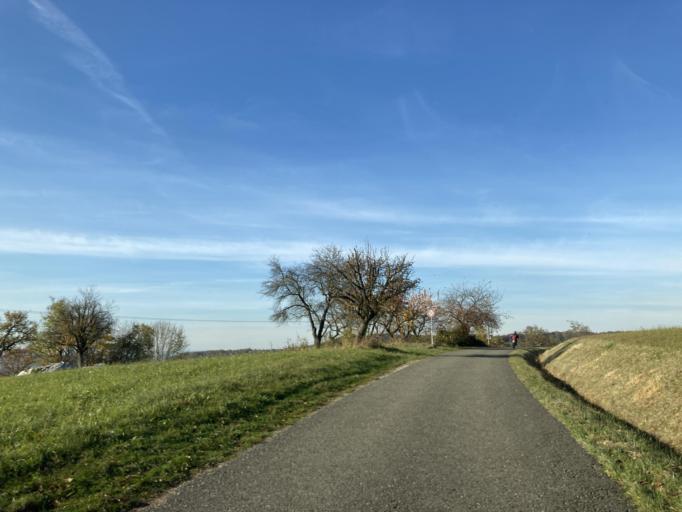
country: DE
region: Baden-Wuerttemberg
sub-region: Tuebingen Region
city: Nehren
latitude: 48.4010
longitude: 9.0963
